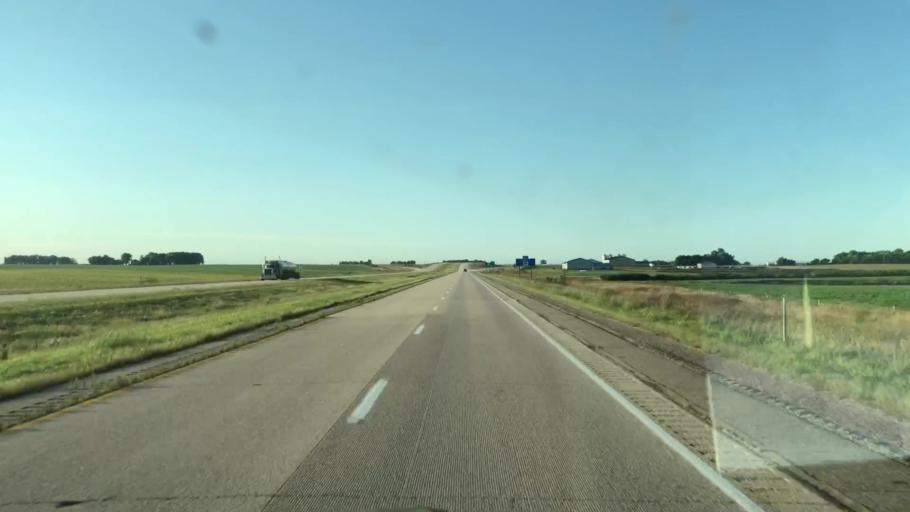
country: US
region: Iowa
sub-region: Osceola County
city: Sibley
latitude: 43.4434
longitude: -95.7137
